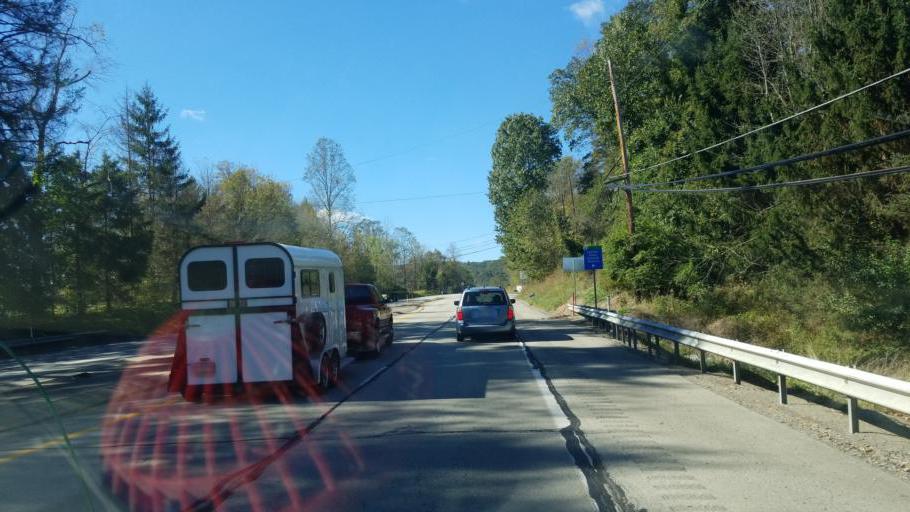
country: US
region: Pennsylvania
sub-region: Westmoreland County
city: Ligonier
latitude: 40.2644
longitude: -79.2821
